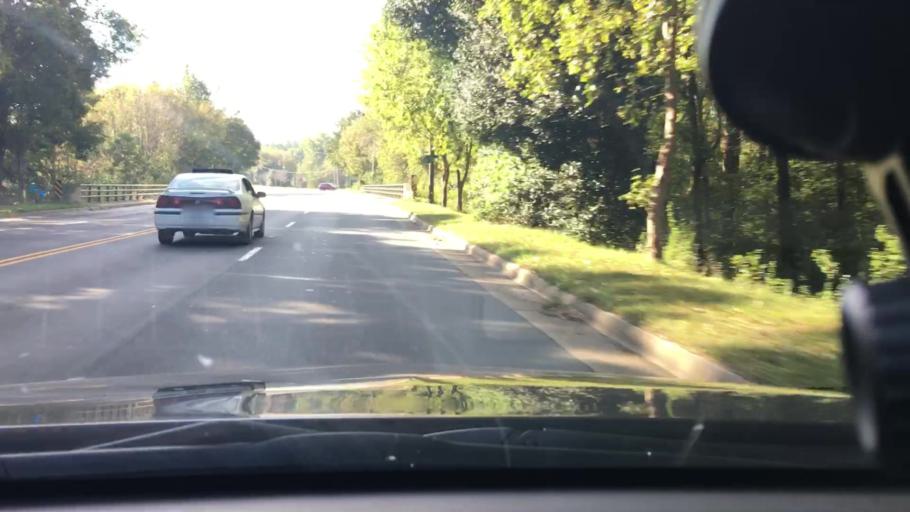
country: US
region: North Carolina
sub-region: Stanly County
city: Albemarle
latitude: 35.3477
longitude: -80.2045
